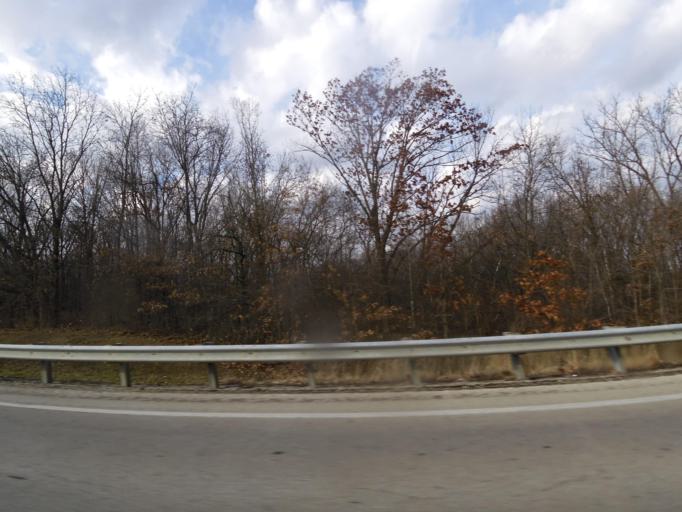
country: US
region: Illinois
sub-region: Christian County
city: Pana
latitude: 39.3108
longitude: -89.0812
